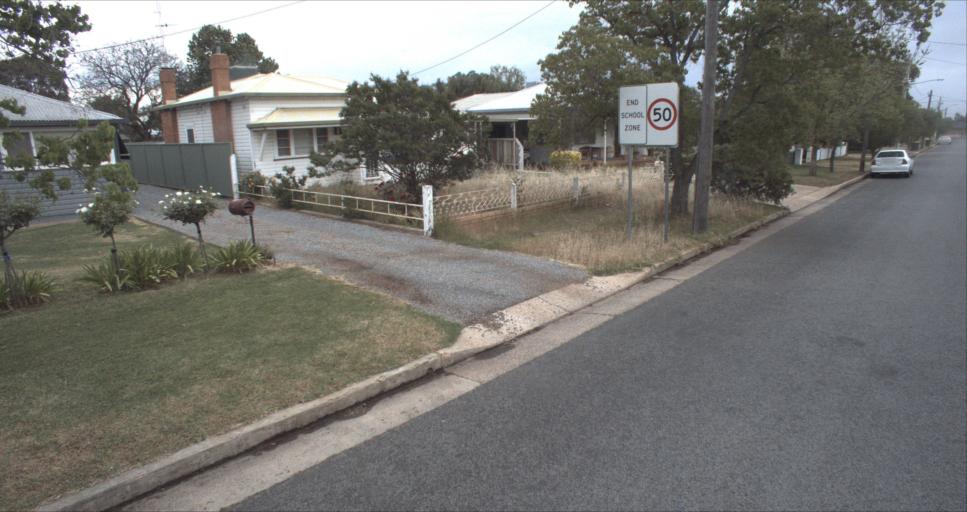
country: AU
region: New South Wales
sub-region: Leeton
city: Leeton
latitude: -34.5473
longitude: 146.4040
